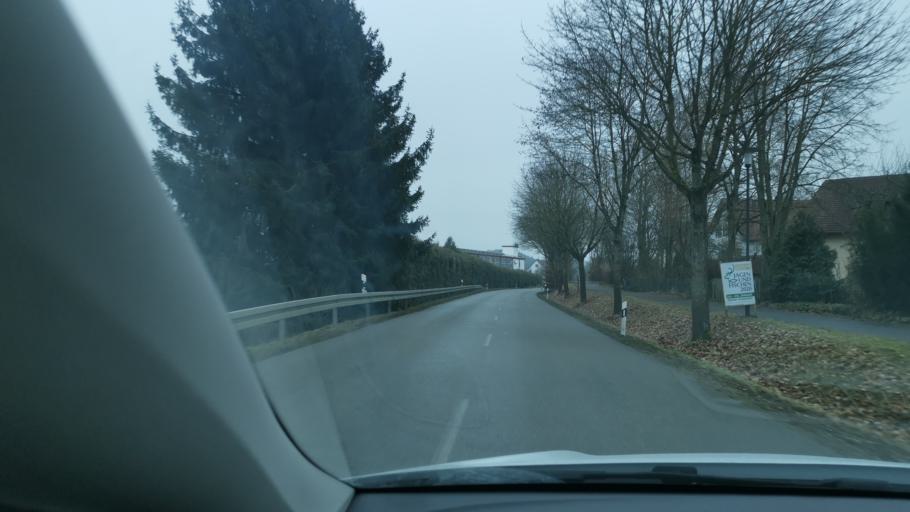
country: DE
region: Bavaria
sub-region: Swabia
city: Holzheim
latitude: 48.5905
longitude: 10.9589
